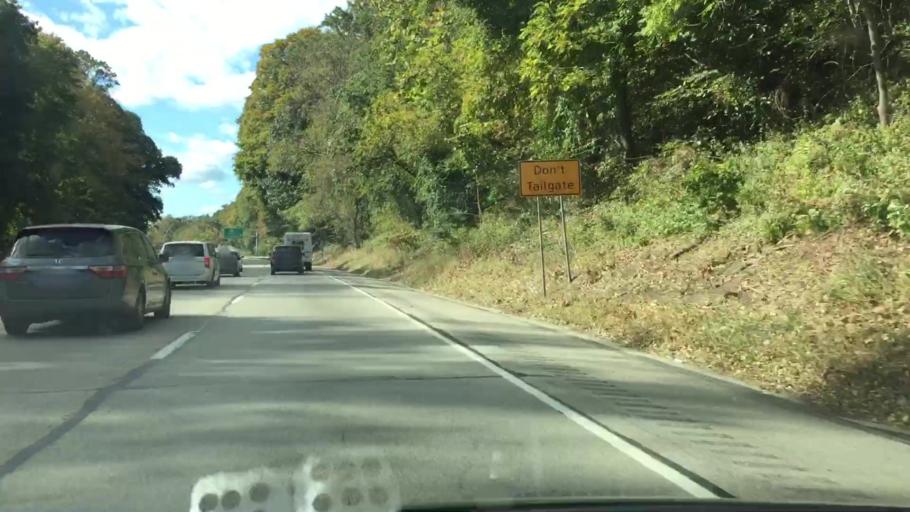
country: US
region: Pennsylvania
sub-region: Delaware County
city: Media
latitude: 39.9367
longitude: -75.3846
